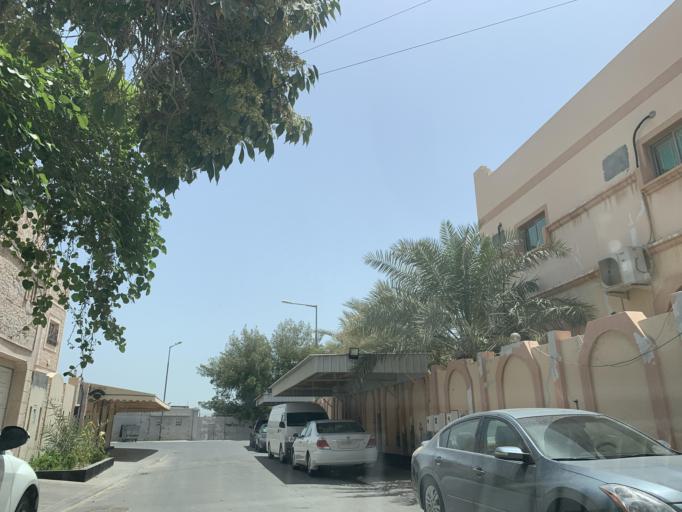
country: BH
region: Northern
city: Madinat `Isa
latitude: 26.1715
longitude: 50.5738
